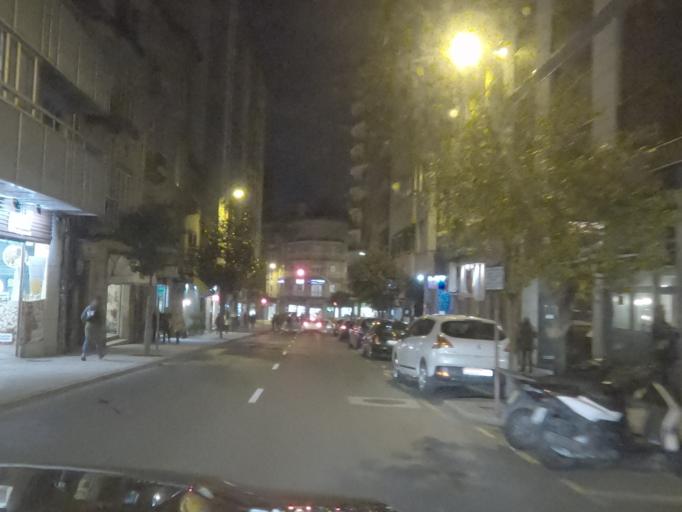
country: ES
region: Galicia
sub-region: Provincia de Ourense
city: Ourense
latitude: 42.3418
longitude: -7.8615
